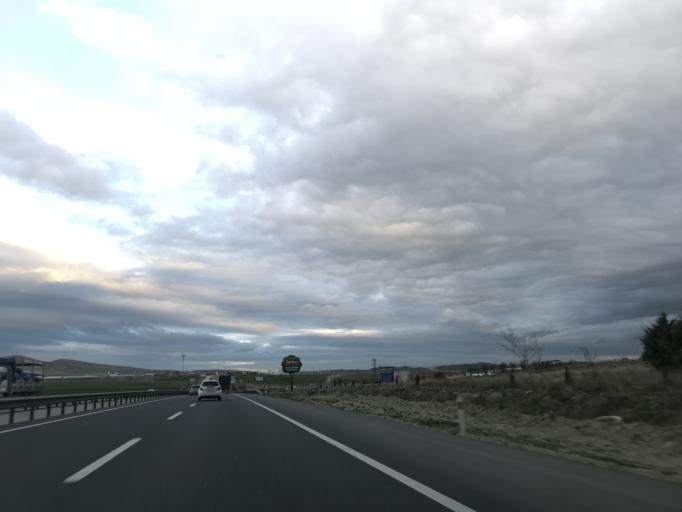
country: TR
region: Ankara
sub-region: Goelbasi
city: Golbasi
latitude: 39.6476
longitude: 32.8195
